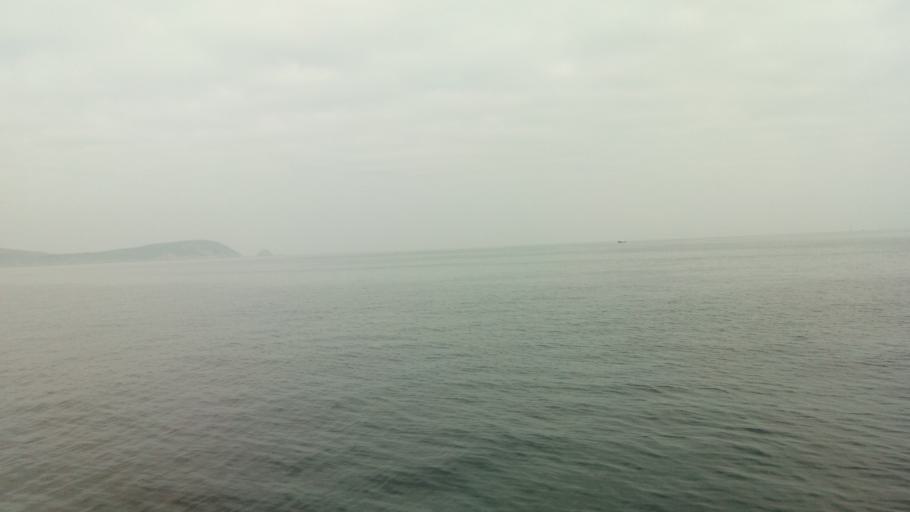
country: ES
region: Galicia
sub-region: Provincia de Pontevedra
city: Sanxenxo
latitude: 42.3796
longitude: -8.8839
